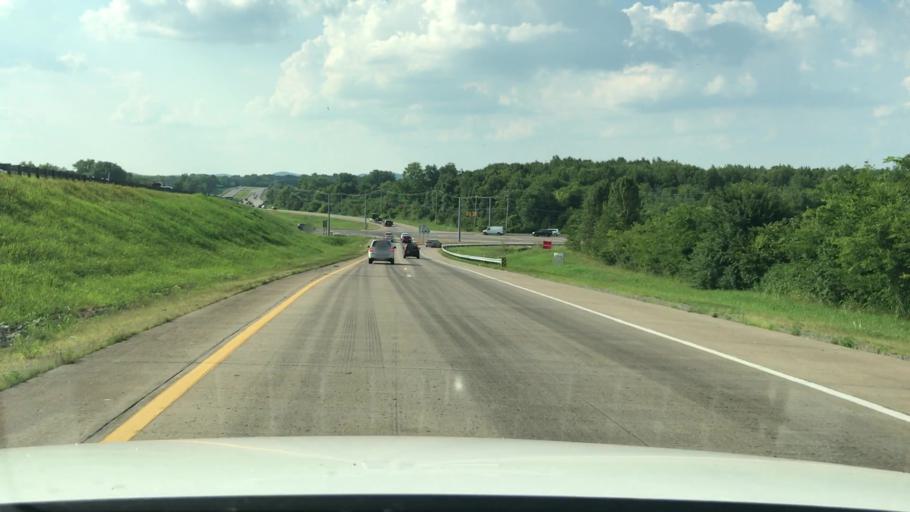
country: US
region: Tennessee
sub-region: Sumner County
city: Gallatin
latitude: 36.3862
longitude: -86.4733
